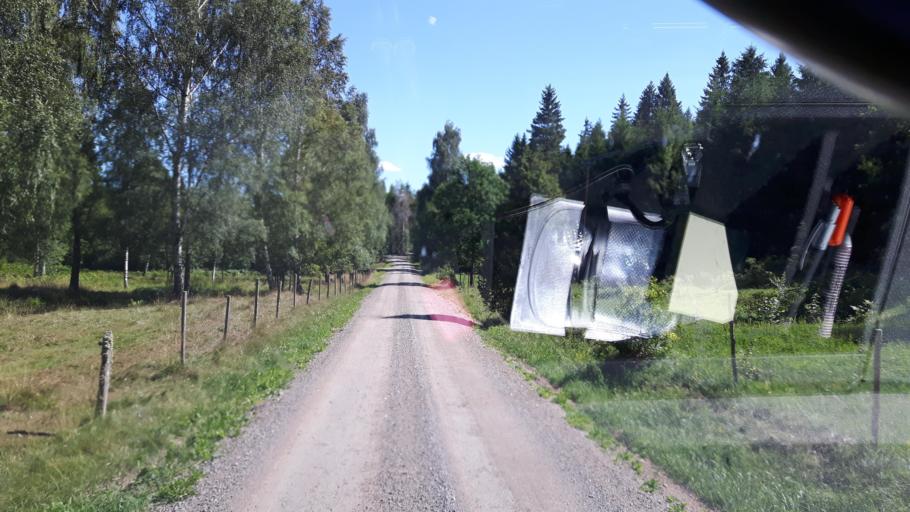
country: SE
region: OEstergoetland
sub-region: Kinda Kommun
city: Kisa
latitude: 58.0064
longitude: 15.6672
